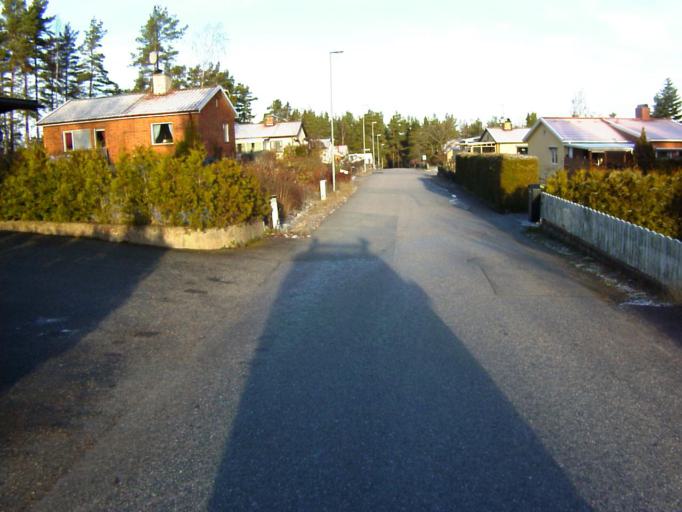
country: SE
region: Soedermanland
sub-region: Eskilstuna Kommun
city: Hallbybrunn
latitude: 59.3938
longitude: 16.4245
